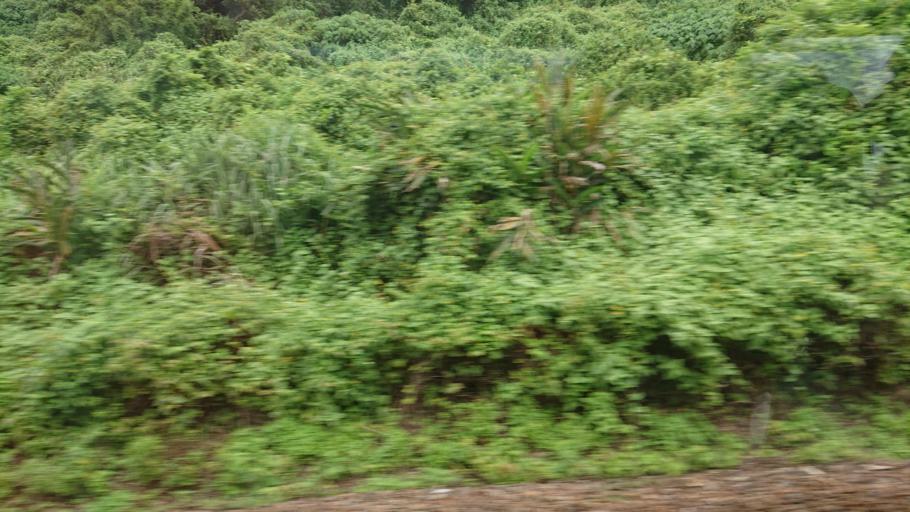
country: TW
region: Taiwan
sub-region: Yilan
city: Yilan
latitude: 24.9126
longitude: 121.8772
